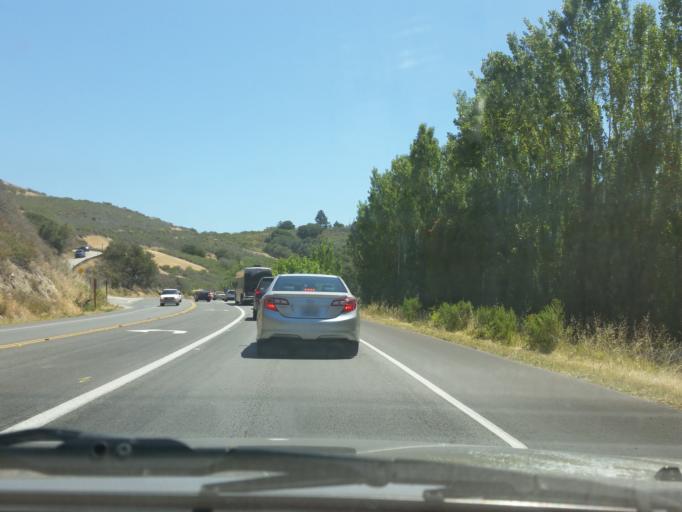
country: US
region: California
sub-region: San Luis Obispo County
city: Avila Beach
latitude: 35.1837
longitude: -120.7239
